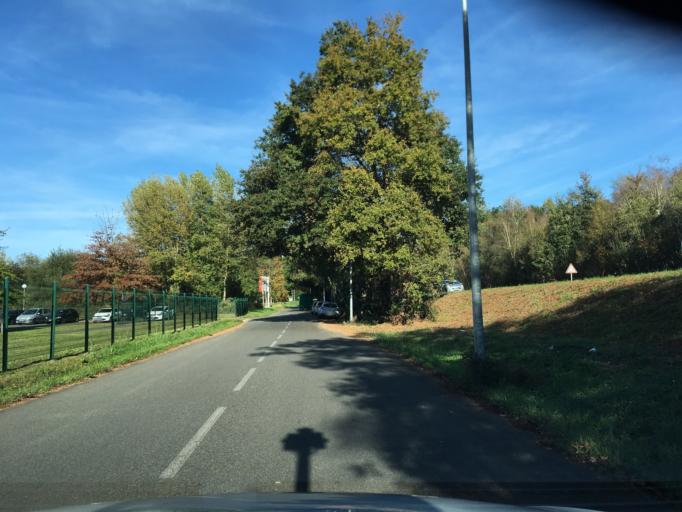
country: FR
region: Aquitaine
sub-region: Departement des Pyrenees-Atlantiques
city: Buros
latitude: 43.3173
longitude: -0.3057
